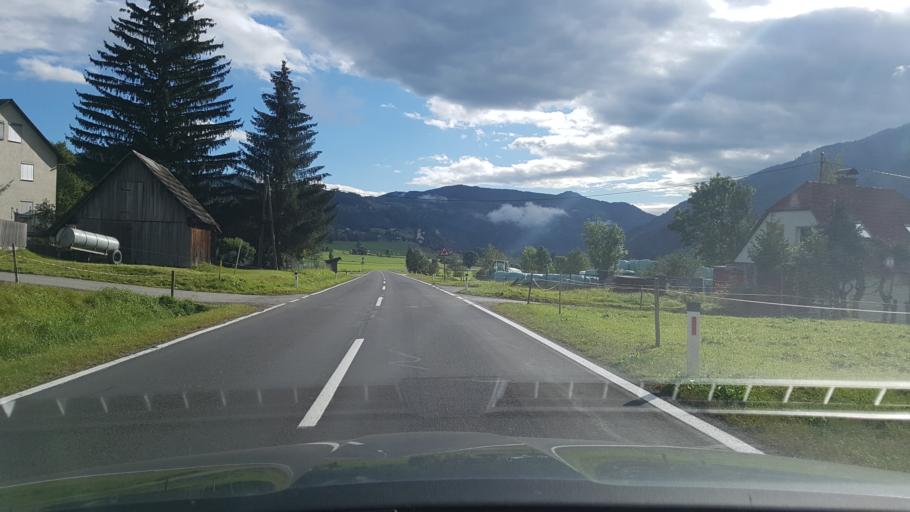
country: AT
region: Styria
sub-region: Politischer Bezirk Murau
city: Sankt Peter am Kammersberg
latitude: 47.1878
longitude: 14.1618
